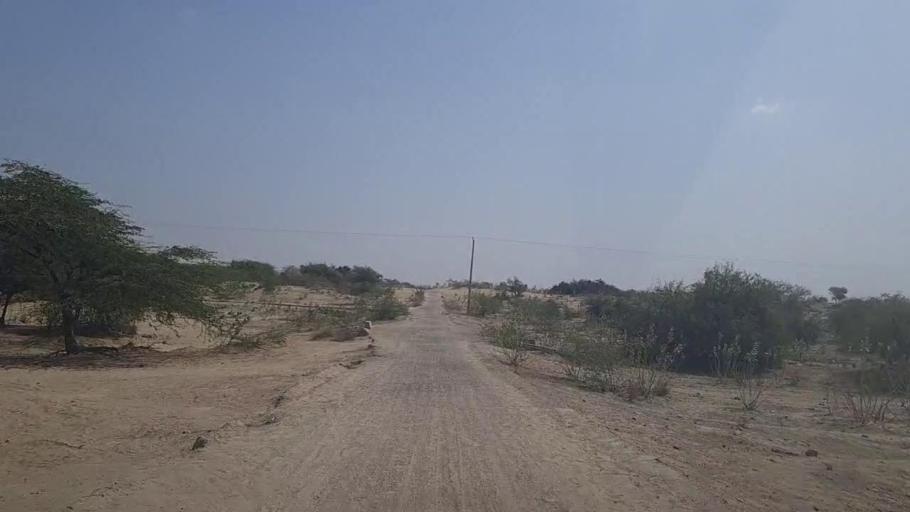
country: PK
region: Sindh
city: Naukot
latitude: 24.8183
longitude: 69.5068
